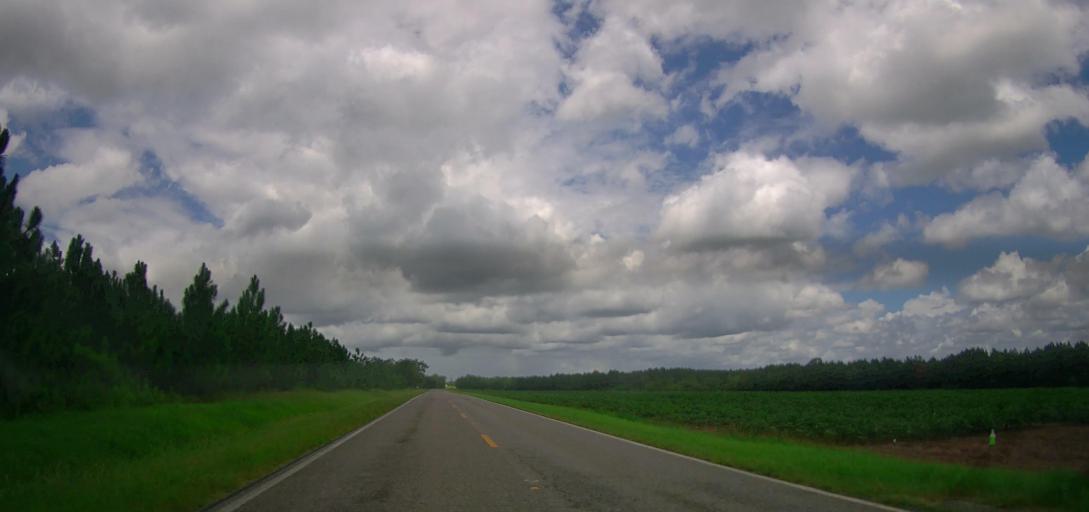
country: US
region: Georgia
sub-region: Wilcox County
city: Rochelle
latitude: 31.8775
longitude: -83.5579
